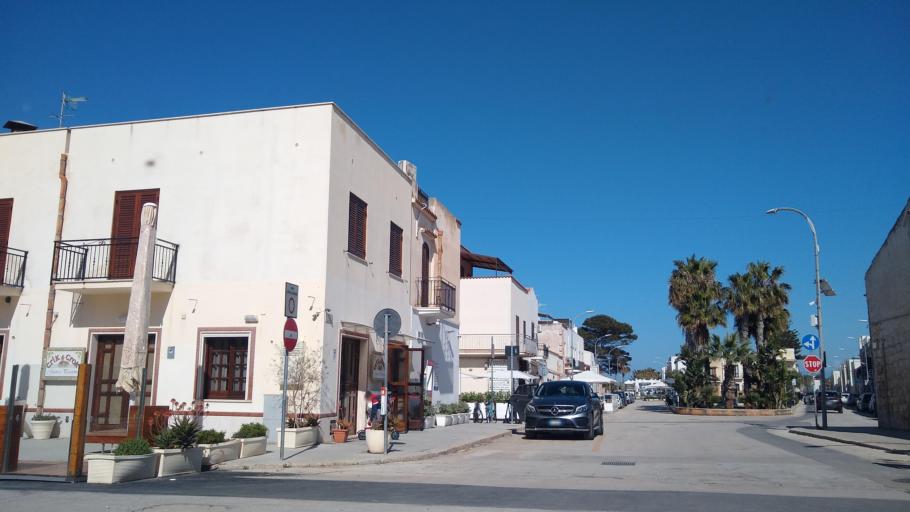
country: IT
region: Sicily
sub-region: Trapani
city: San Vito Lo Capo
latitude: 38.1752
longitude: 12.7359
